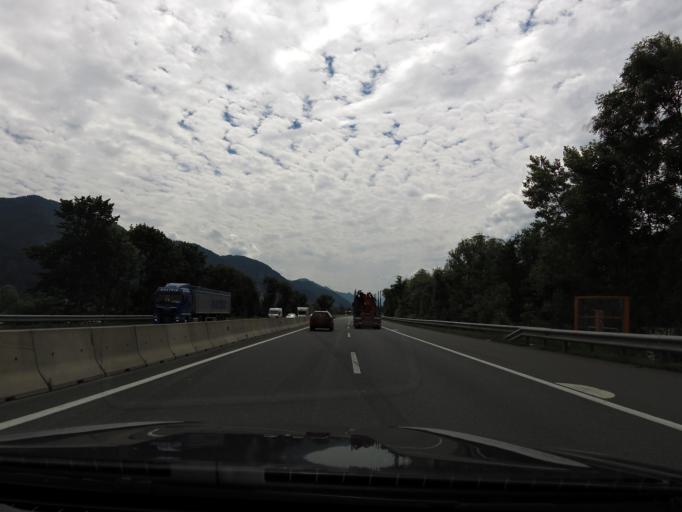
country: AT
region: Tyrol
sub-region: Politischer Bezirk Kufstein
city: Worgl
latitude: 47.4889
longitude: 12.0494
